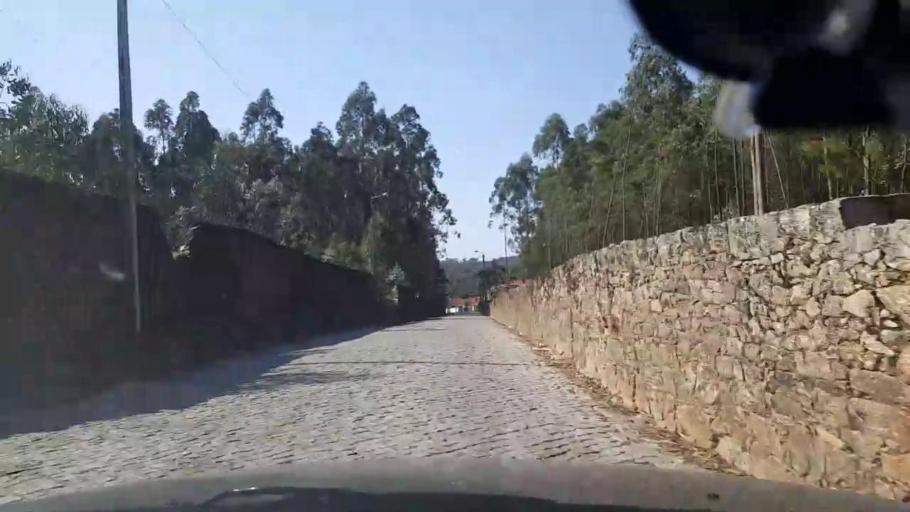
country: PT
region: Porto
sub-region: Povoa de Varzim
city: Pedroso
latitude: 41.4030
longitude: -8.7034
